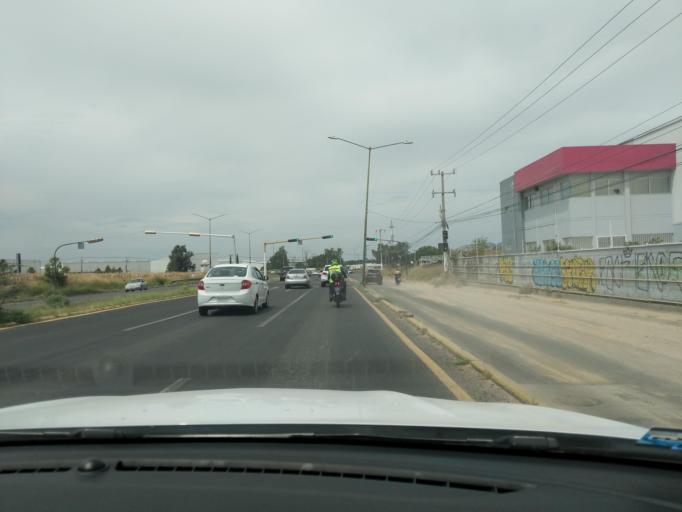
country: MX
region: Jalisco
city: Tesistan
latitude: 20.7901
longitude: -103.4748
